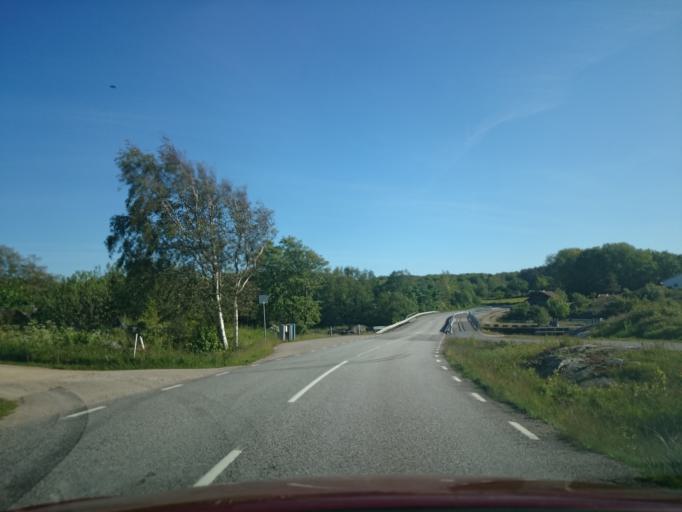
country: SE
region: Vaestra Goetaland
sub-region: Lysekils Kommun
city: Lysekil
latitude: 58.2436
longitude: 11.4690
